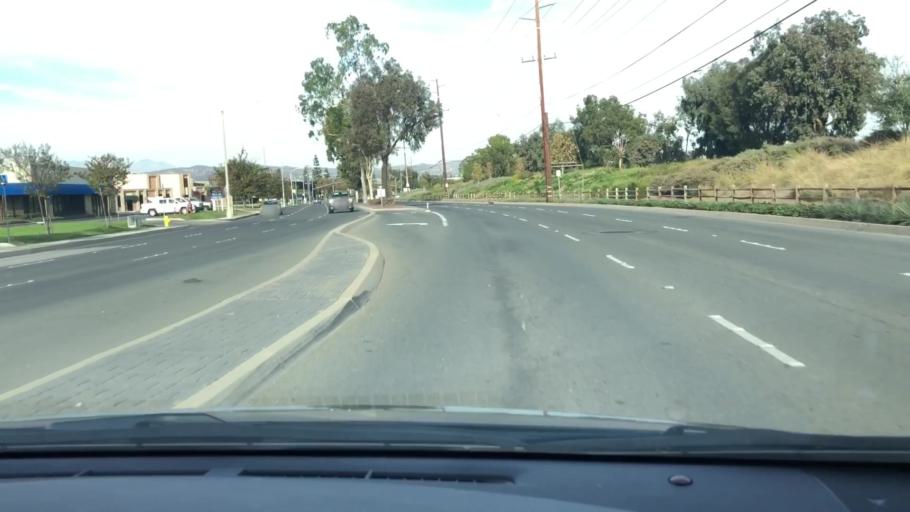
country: US
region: California
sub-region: Orange County
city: Yorba Linda
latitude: 33.8562
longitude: -117.8330
